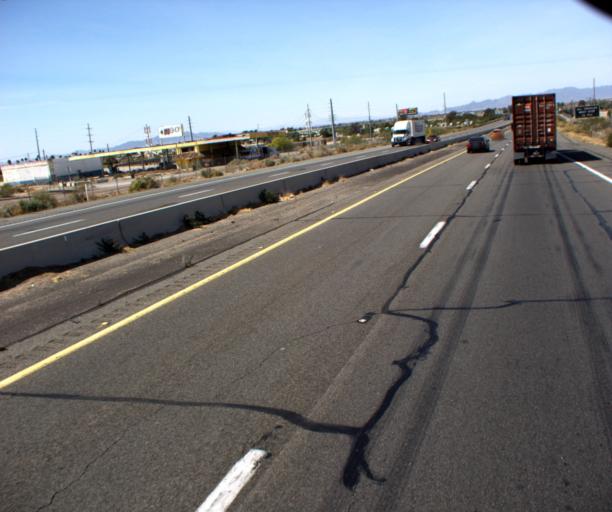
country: US
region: Arizona
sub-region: La Paz County
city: Ehrenberg
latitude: 33.6034
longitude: -114.5247
